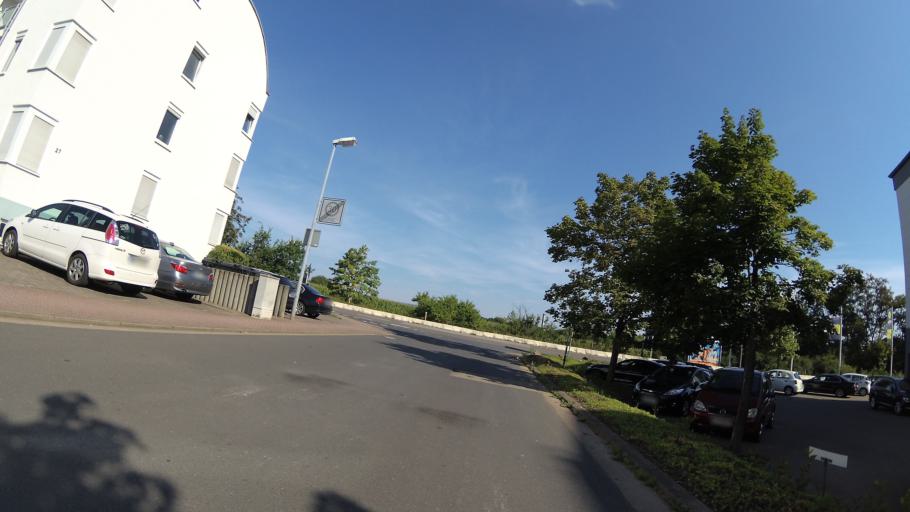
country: DE
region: Saarland
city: Homburg
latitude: 49.3399
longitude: 7.3307
